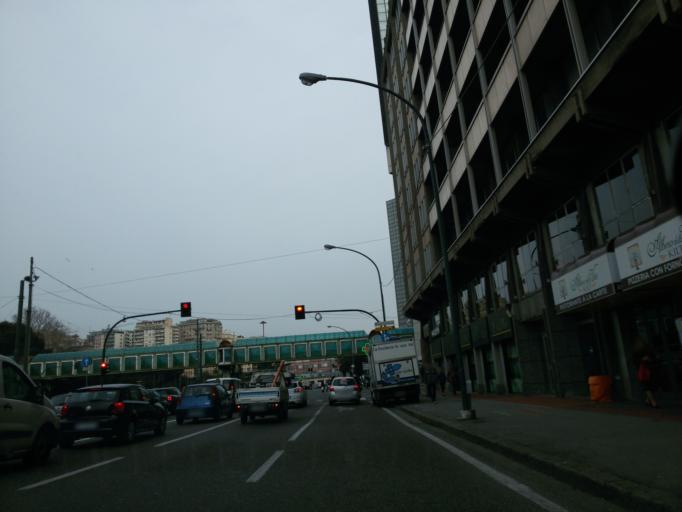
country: IT
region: Liguria
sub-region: Provincia di Genova
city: San Teodoro
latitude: 44.4034
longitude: 8.9471
